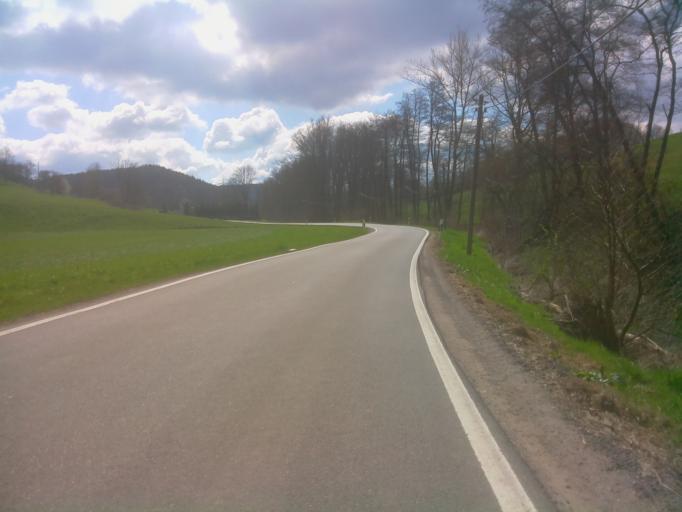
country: DE
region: Thuringia
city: Karlsdorf
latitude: 50.8040
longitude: 11.7936
